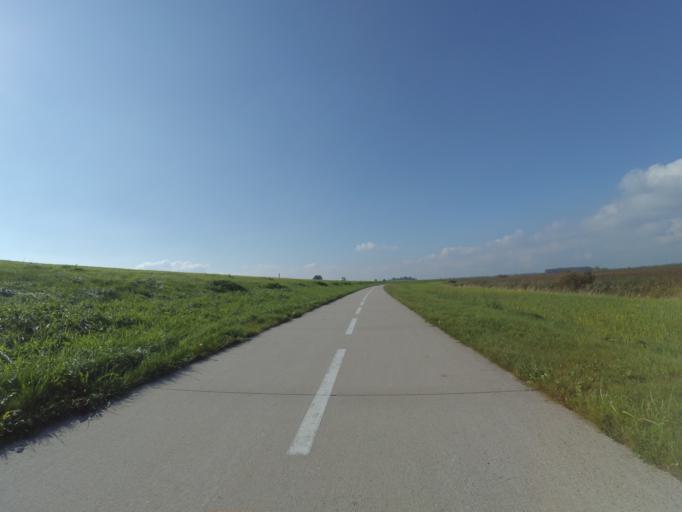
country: NL
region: Gelderland
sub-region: Gemeente Harderwijk
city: Harderwijk
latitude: 52.3634
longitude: 5.5873
